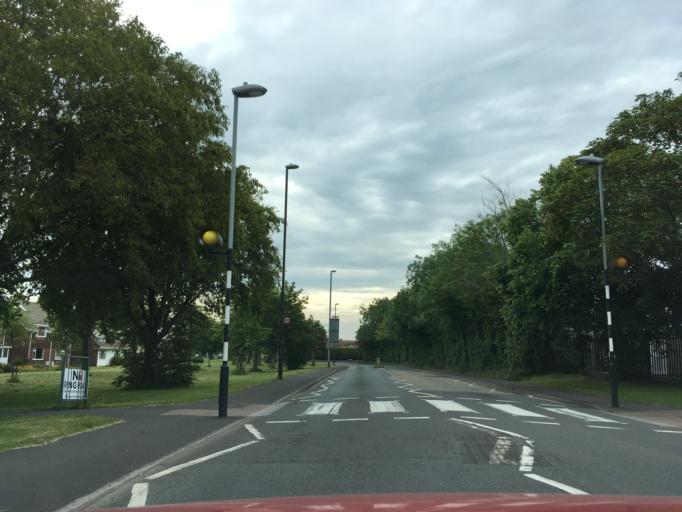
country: GB
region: England
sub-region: Bath and North East Somerset
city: Whitchurch
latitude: 51.4070
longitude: -2.5706
